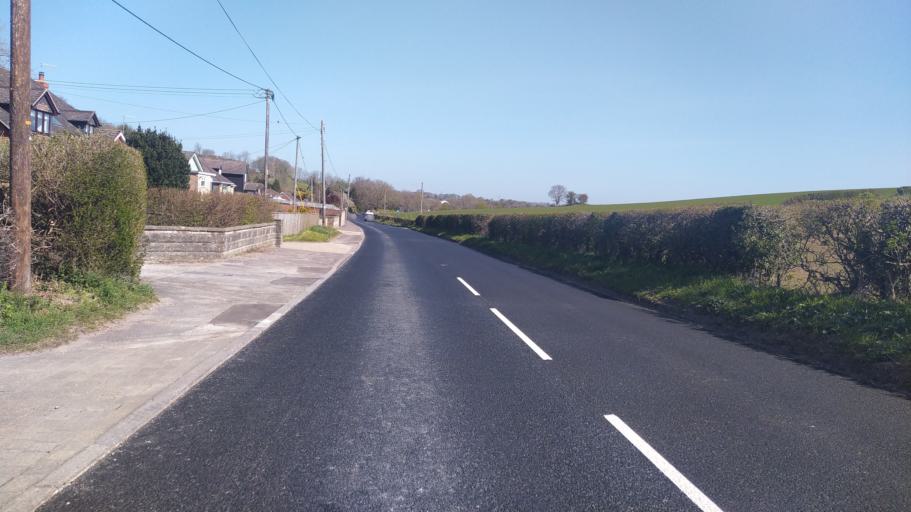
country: GB
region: England
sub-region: Wiltshire
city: Wilton
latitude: 51.0306
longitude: -1.8490
